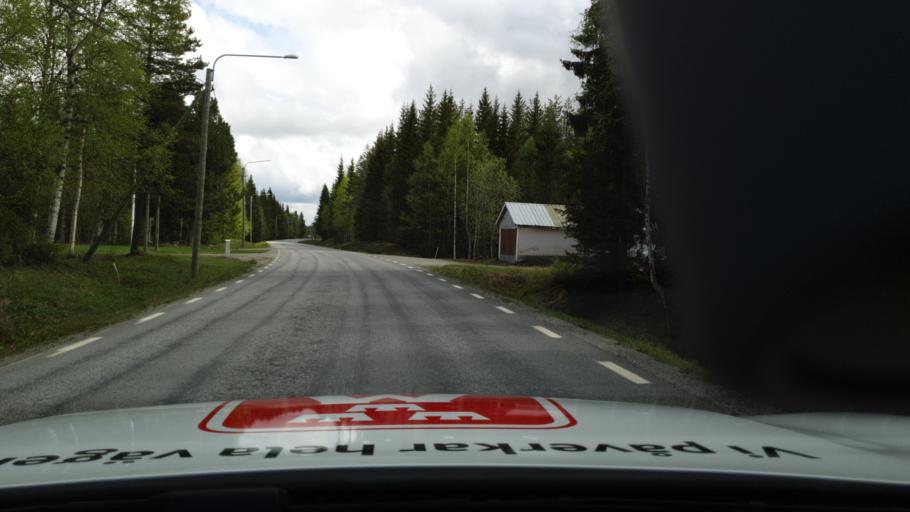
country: SE
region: Vaesterbotten
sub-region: Vilhelmina Kommun
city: Sjoberg
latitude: 64.6524
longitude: 16.3255
